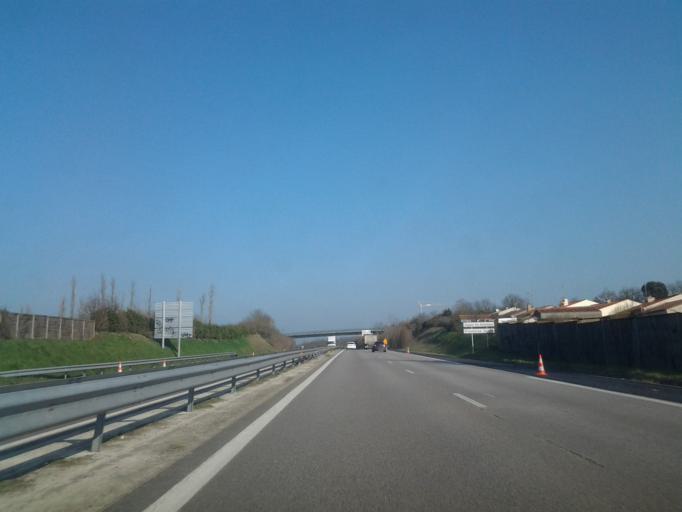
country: FR
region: Pays de la Loire
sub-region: Departement de la Vendee
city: Aizenay
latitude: 46.7414
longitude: -1.6216
